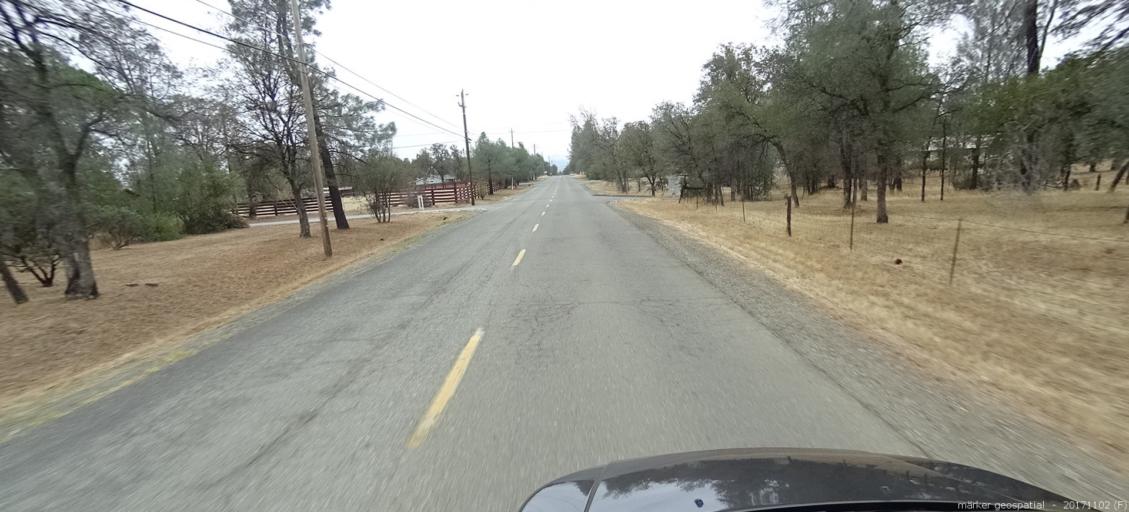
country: US
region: California
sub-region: Shasta County
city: Bella Vista
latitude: 40.6227
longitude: -122.2966
